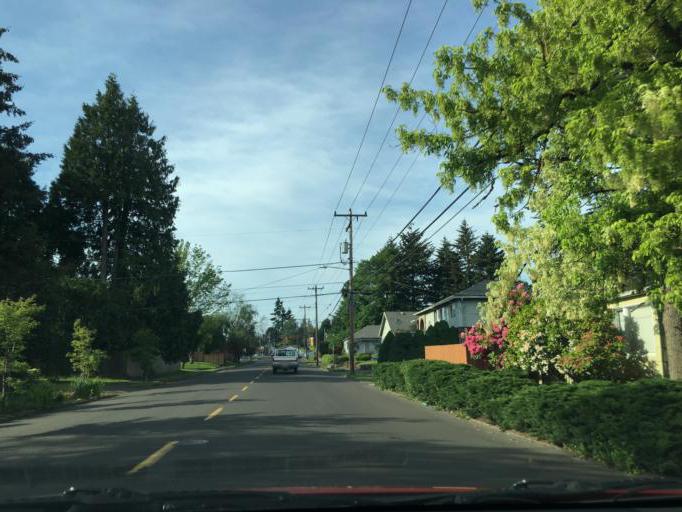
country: US
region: Oregon
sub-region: Multnomah County
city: Lents
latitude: 45.5168
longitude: -122.5692
